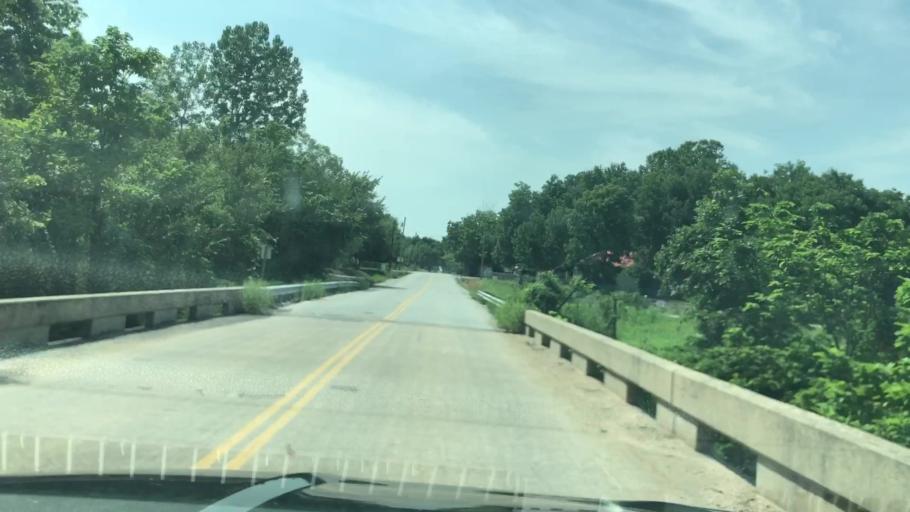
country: US
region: Oklahoma
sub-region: Ottawa County
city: Commerce
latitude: 36.9291
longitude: -94.8590
